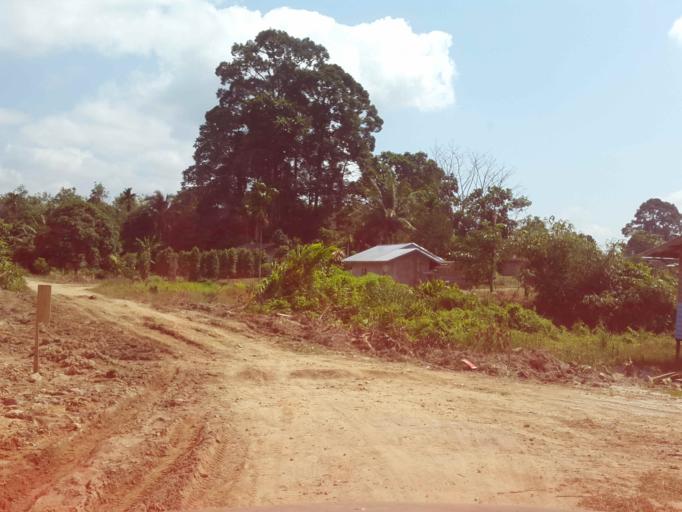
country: MY
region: Sarawak
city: Simanggang
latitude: 0.9617
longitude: 111.2928
